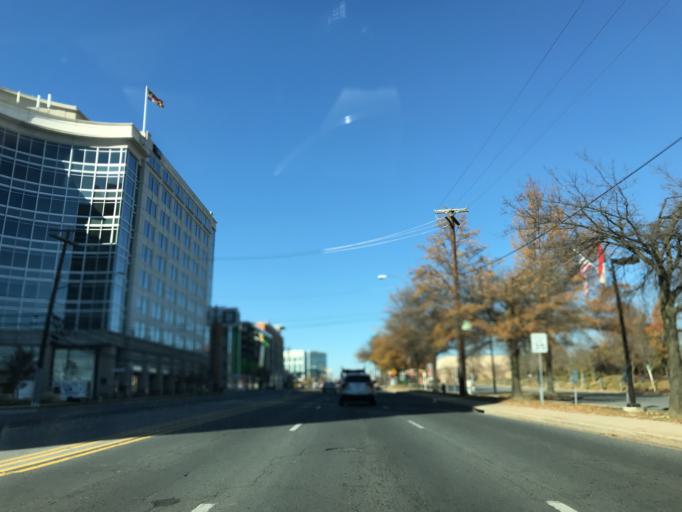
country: US
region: Maryland
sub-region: Montgomery County
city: Rockville
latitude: 39.0856
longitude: -77.1486
